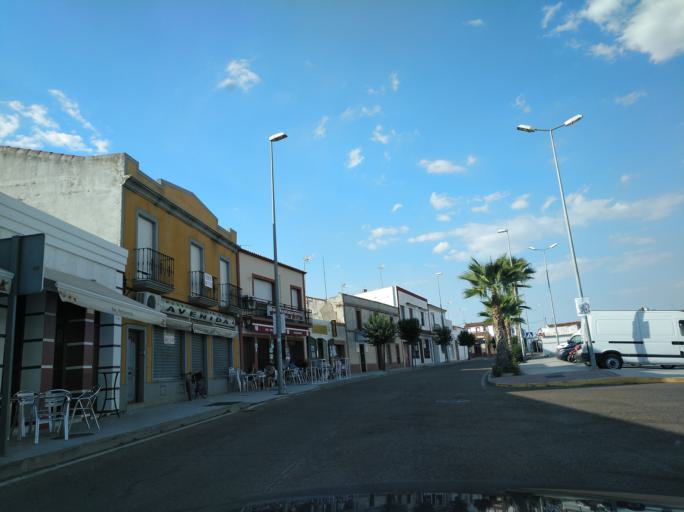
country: ES
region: Extremadura
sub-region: Provincia de Badajoz
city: Alconchel
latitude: 38.5143
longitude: -7.0694
